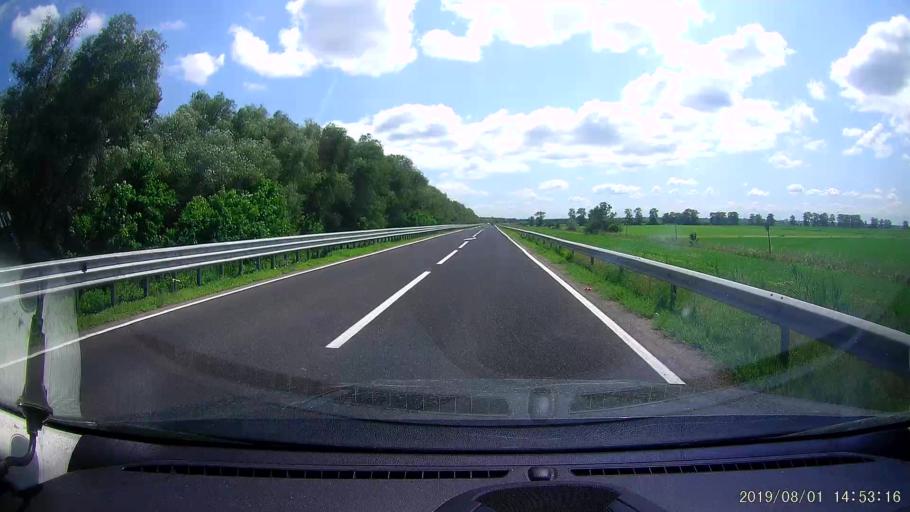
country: RO
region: Braila
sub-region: Municipiul Braila
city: Braila
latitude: 45.3391
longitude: 28.0050
